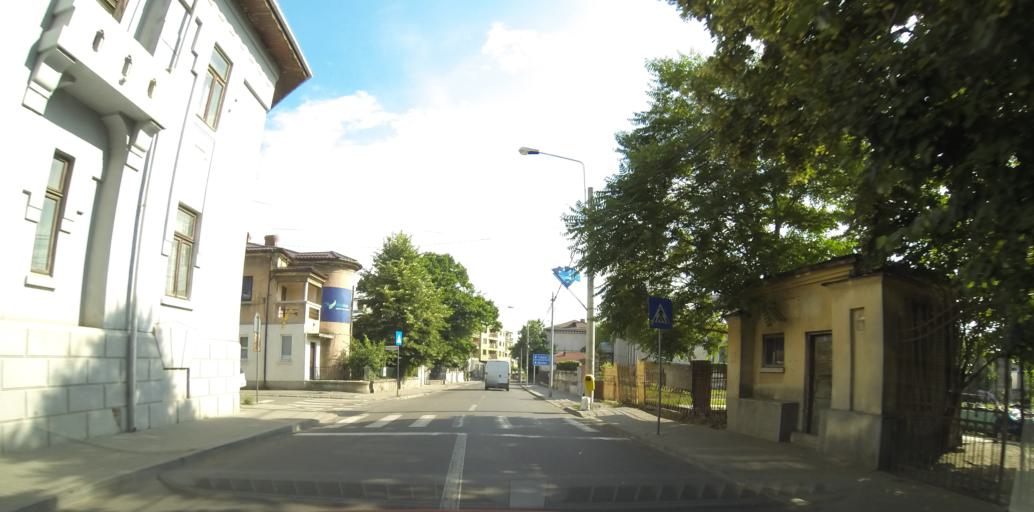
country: RO
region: Dolj
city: Craiova
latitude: 44.3130
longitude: 23.7989
